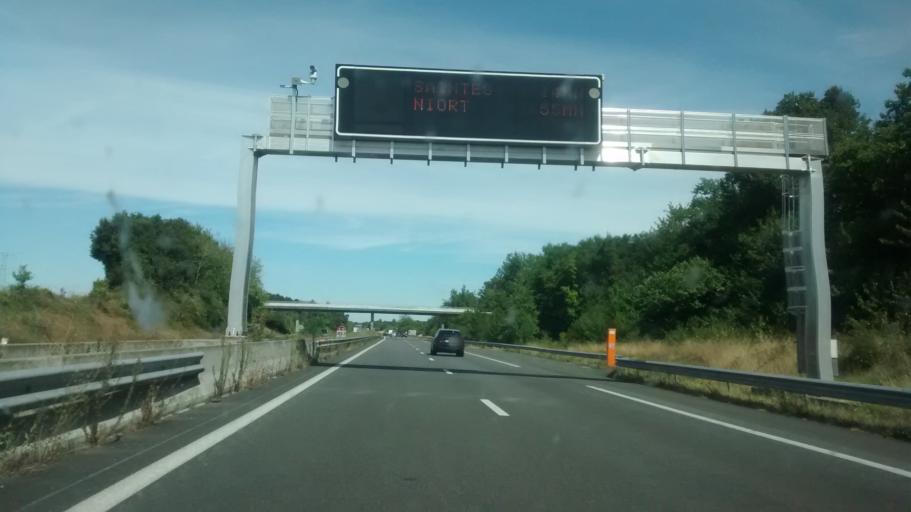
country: FR
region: Poitou-Charentes
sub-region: Departement de la Charente-Maritime
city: Pons
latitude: 45.5529
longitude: -0.6034
